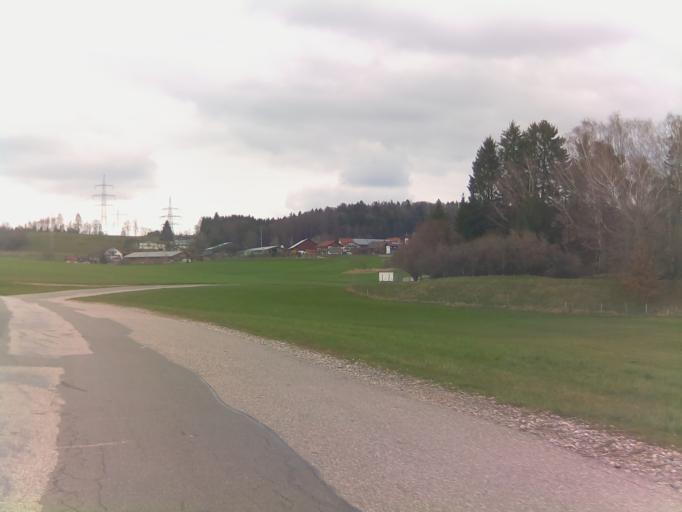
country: DE
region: Bavaria
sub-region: Upper Bavaria
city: Pahl
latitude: 47.8977
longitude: 11.2199
